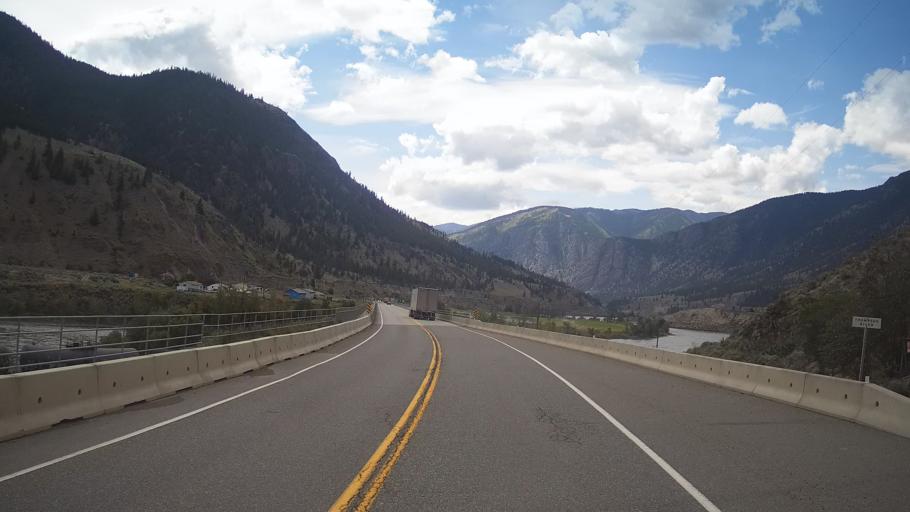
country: CA
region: British Columbia
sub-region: Thompson-Nicola Regional District
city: Ashcroft
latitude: 50.4202
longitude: -121.3529
